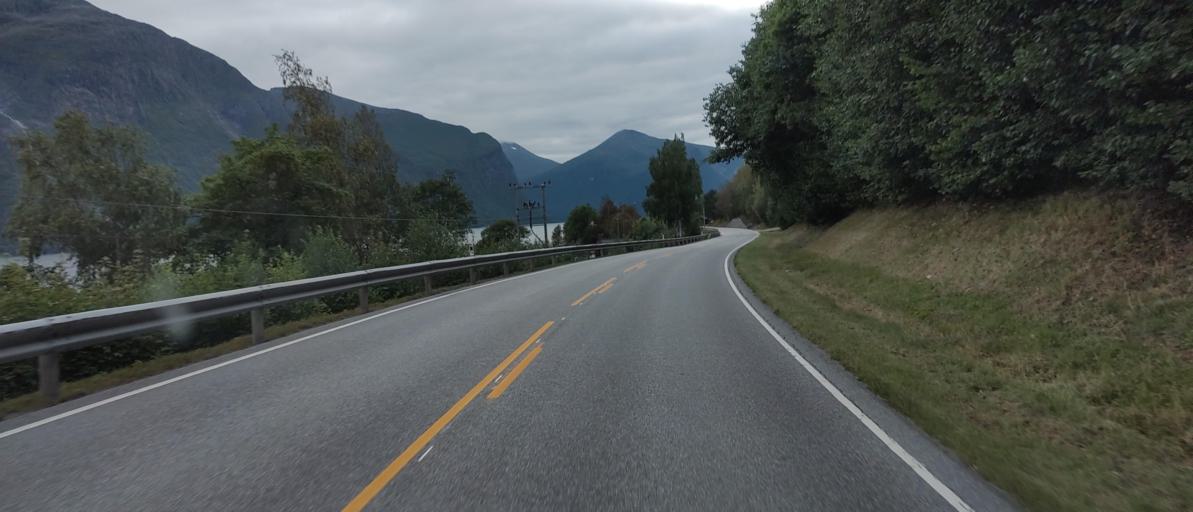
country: NO
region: More og Romsdal
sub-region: Rauma
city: Andalsnes
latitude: 62.5721
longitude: 7.6542
